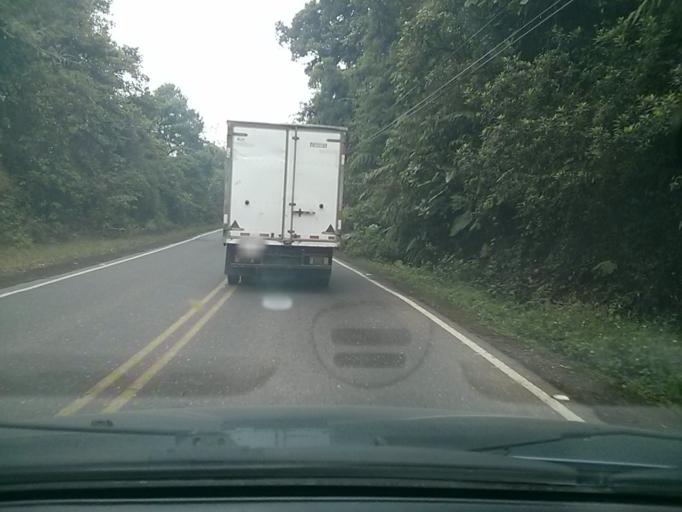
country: CR
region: San Jose
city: San Marcos
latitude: 9.7391
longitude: -83.9539
